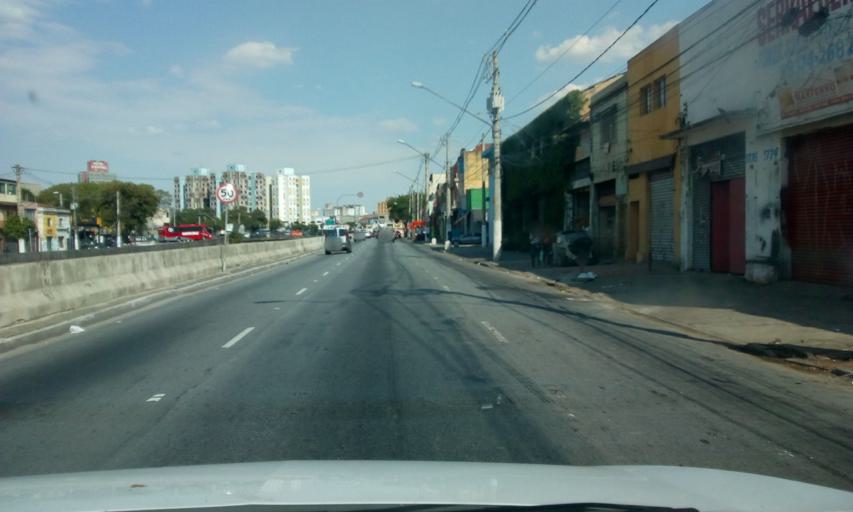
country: BR
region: Sao Paulo
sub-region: Sao Paulo
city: Sao Paulo
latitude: -23.5304
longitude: -46.6269
